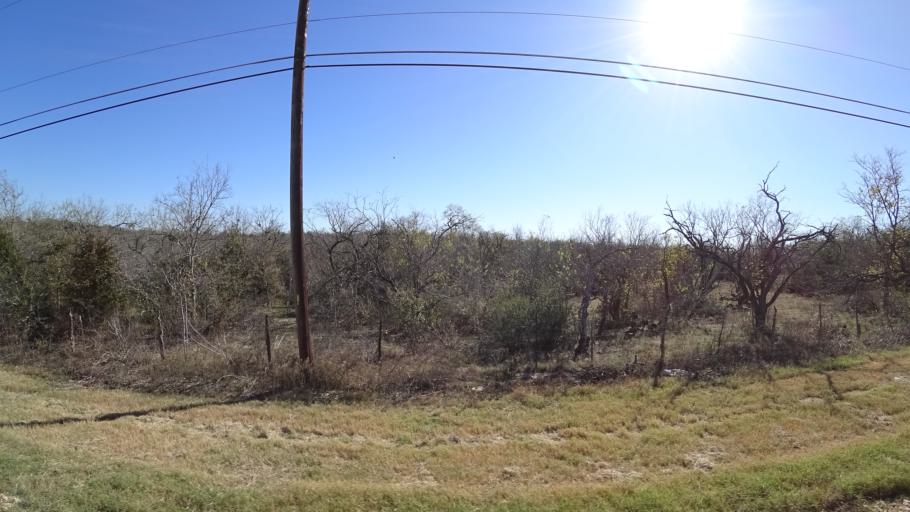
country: US
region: Texas
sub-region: Travis County
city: Garfield
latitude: 30.1213
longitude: -97.6445
